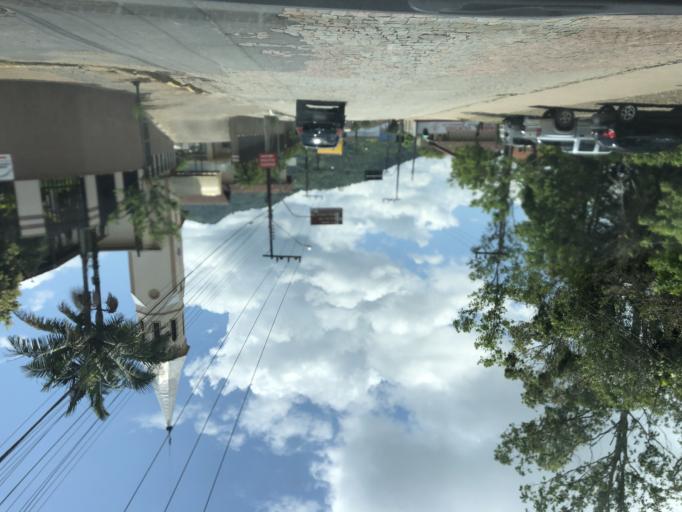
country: BR
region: Santa Catarina
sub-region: Jaragua Do Sul
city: Jaragua do Sul
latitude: -26.5149
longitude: -49.1292
